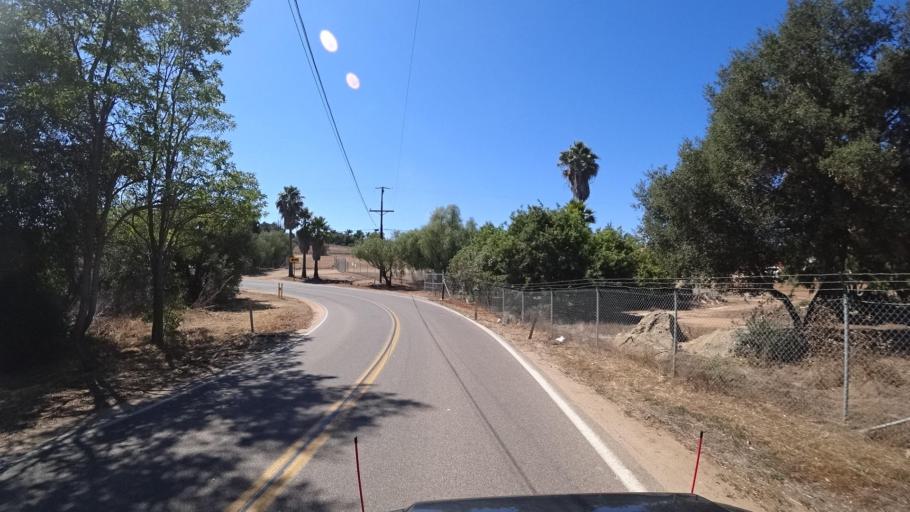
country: US
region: California
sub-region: San Diego County
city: Hidden Meadows
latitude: 33.2696
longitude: -117.1084
